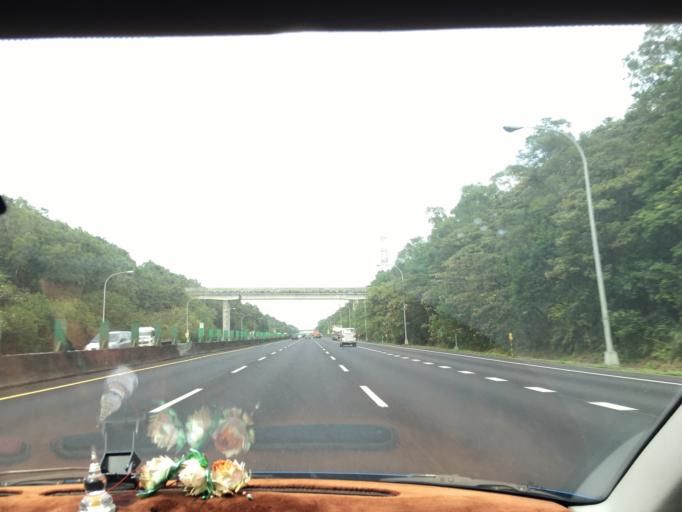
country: TW
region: Taiwan
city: Daxi
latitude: 24.8154
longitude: 121.2005
